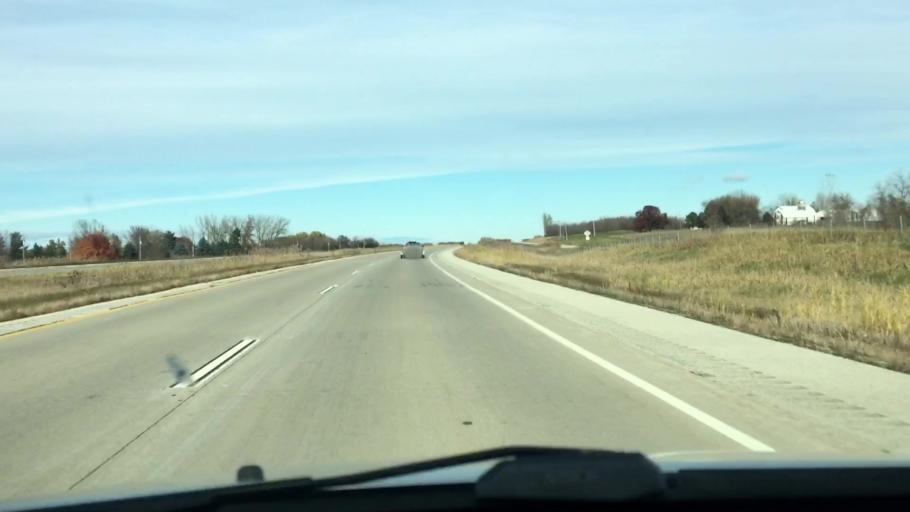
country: US
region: Wisconsin
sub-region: Kewaunee County
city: Luxemburg
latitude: 44.6502
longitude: -87.7519
